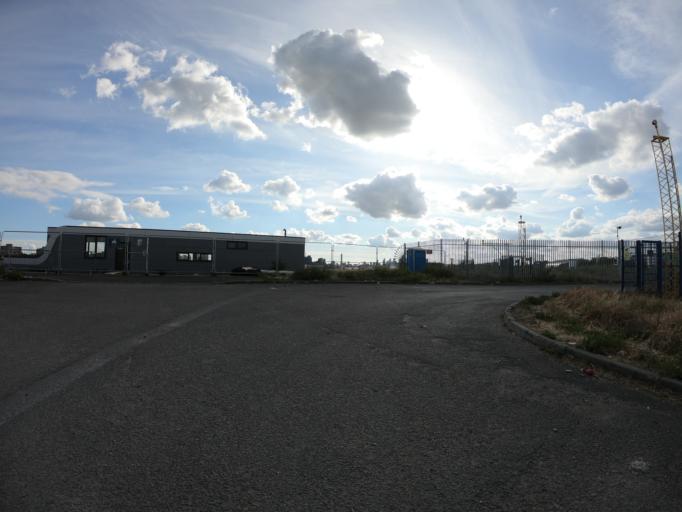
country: GB
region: England
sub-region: Greater London
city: Woolwich
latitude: 51.5047
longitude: 0.0692
